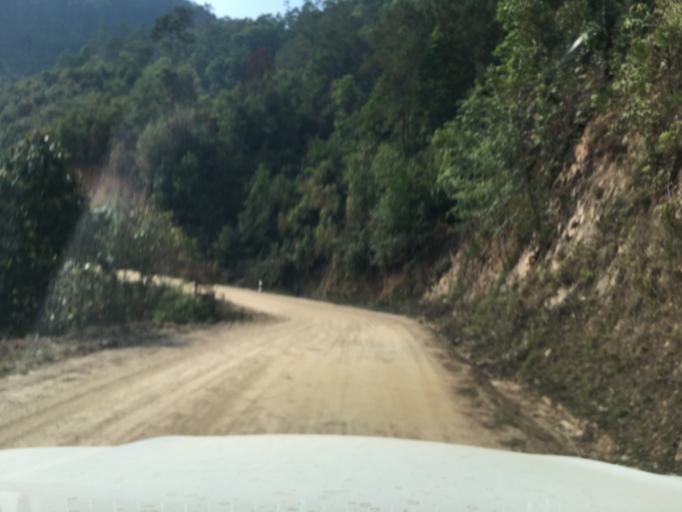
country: LA
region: Houaphan
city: Huameung
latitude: 20.2052
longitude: 103.8518
